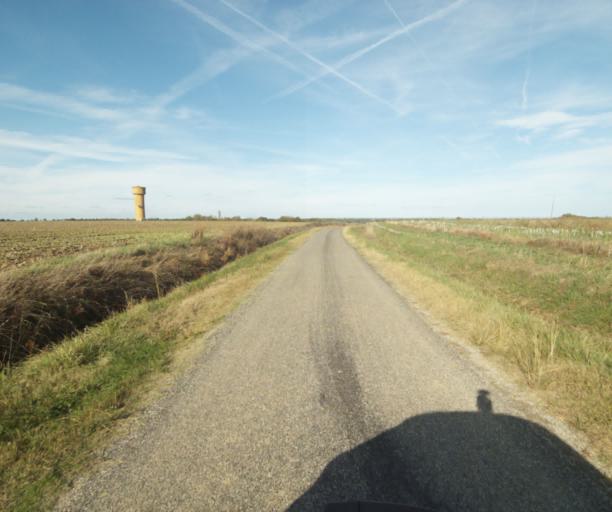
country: FR
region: Midi-Pyrenees
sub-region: Departement du Tarn-et-Garonne
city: Finhan
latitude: 43.9232
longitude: 1.1356
